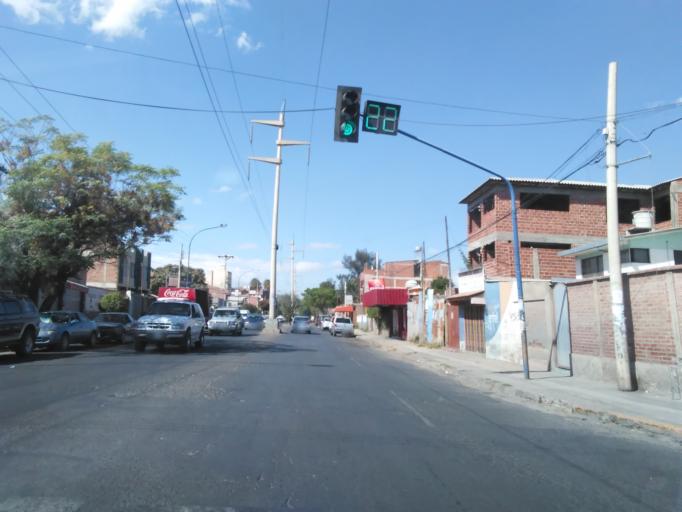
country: BO
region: Cochabamba
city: Cochabamba
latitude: -17.3965
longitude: -66.1741
